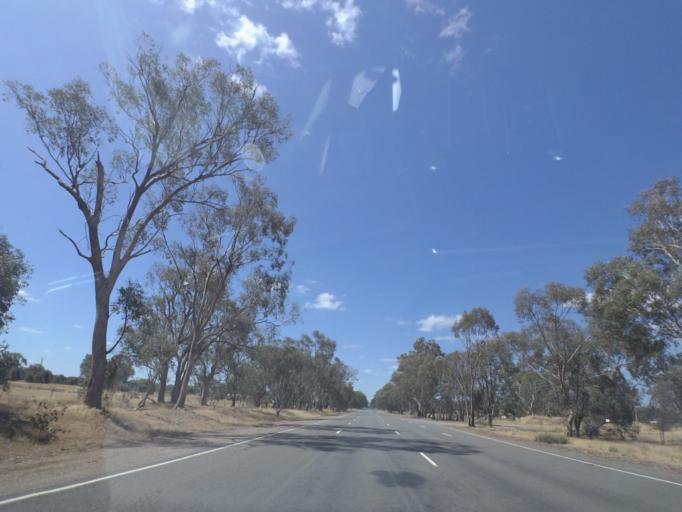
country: AU
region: Victoria
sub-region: Wangaratta
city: Wangaratta
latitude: -36.4302
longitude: 146.2540
